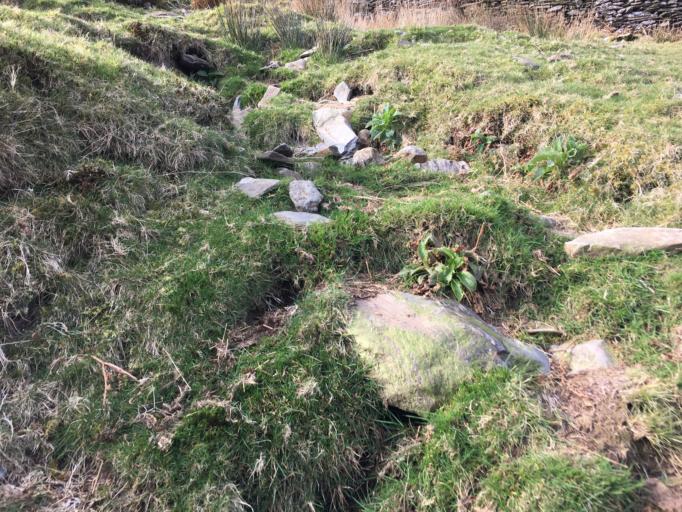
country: GB
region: Wales
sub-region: Gwynedd
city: Porthmadog
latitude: 53.0096
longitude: -4.1271
